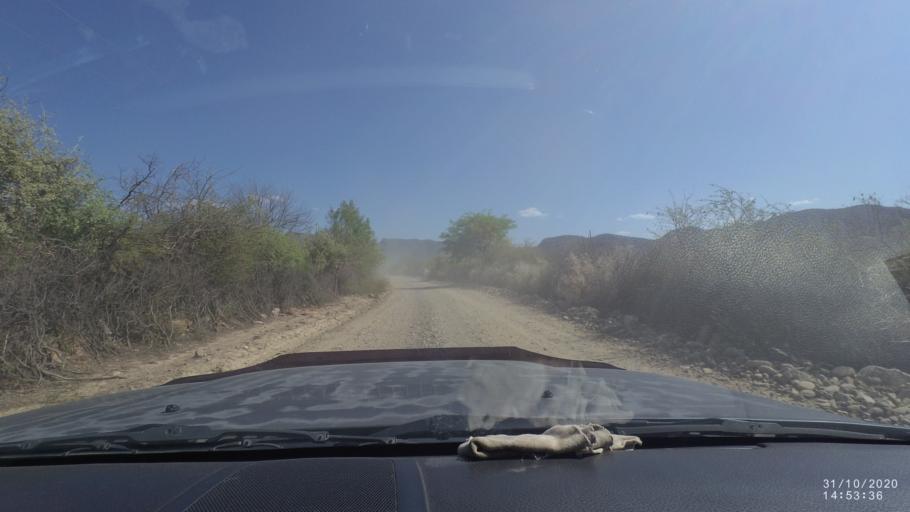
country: BO
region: Cochabamba
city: Aiquile
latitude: -18.2204
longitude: -64.8575
